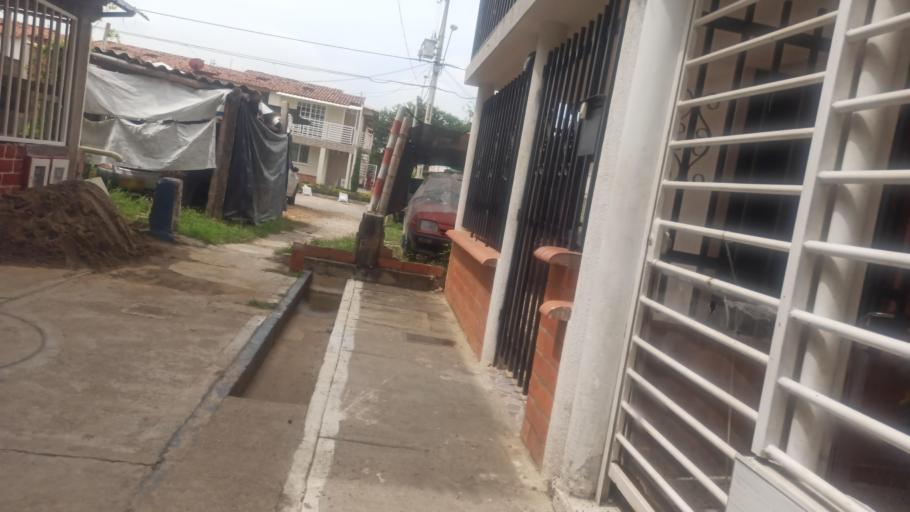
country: CO
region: Valle del Cauca
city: Jamundi
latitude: 3.2344
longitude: -76.5097
